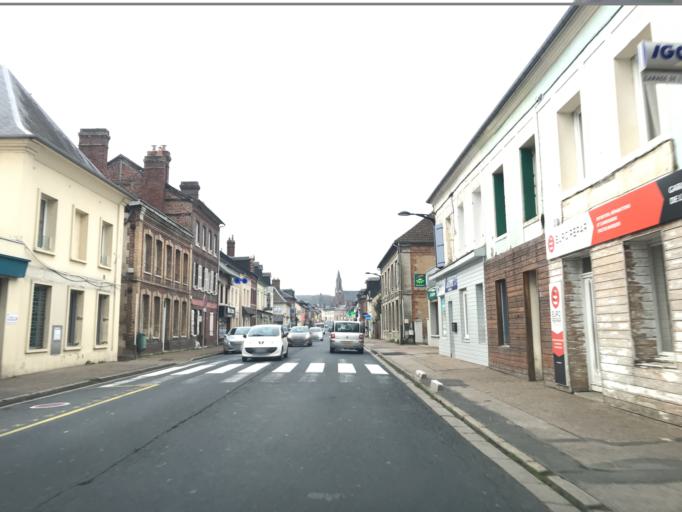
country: FR
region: Haute-Normandie
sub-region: Departement de l'Eure
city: Fleury-sur-Andelle
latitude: 49.3597
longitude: 1.3579
